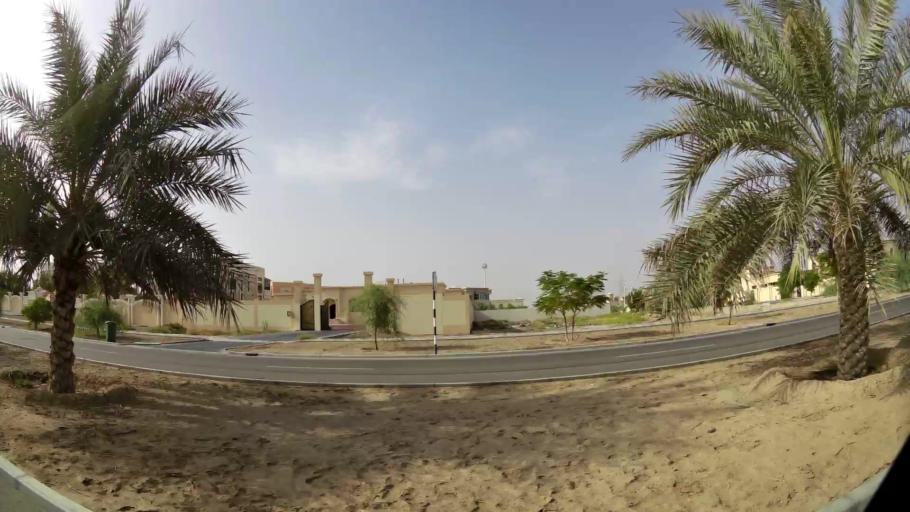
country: AE
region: Abu Dhabi
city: Al Ain
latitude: 24.1529
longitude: 55.7153
